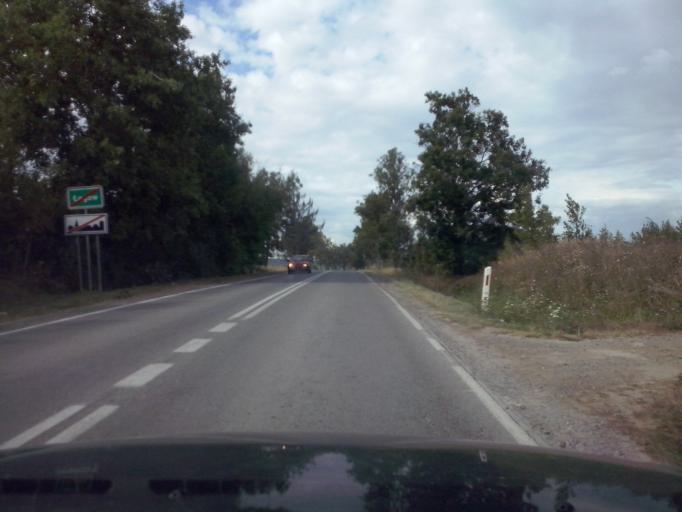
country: PL
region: Swietokrzyskie
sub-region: Powiat kielecki
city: Lagow
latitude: 50.7836
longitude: 21.0822
